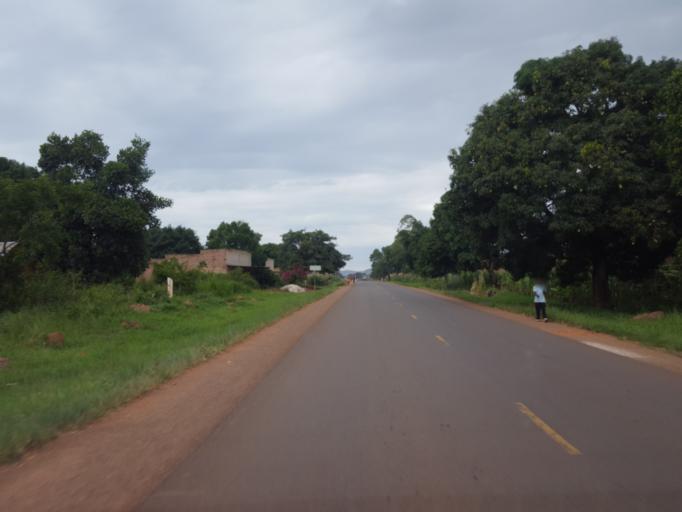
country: UG
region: Central Region
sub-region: Kiboga District
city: Kiboga
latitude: 1.0331
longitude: 31.6767
